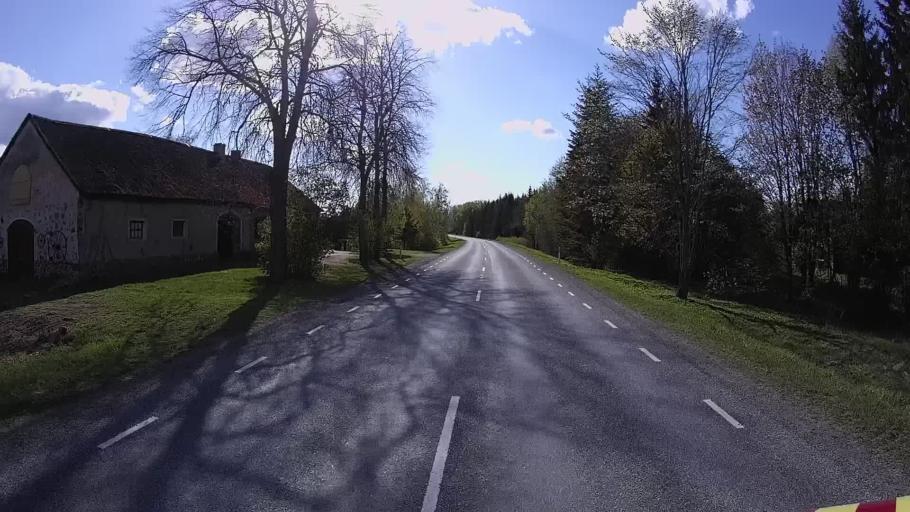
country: EE
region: Jogevamaa
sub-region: Poltsamaa linn
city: Poltsamaa
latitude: 58.6788
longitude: 26.0367
